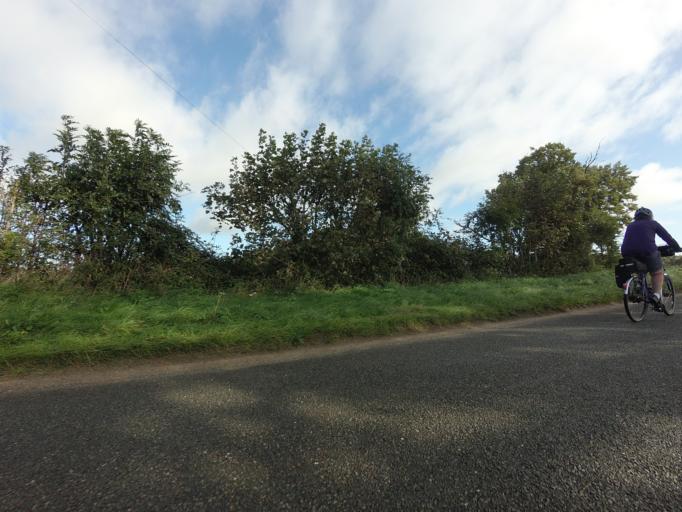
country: GB
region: England
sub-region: Norfolk
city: Dersingham
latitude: 52.8623
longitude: 0.6657
